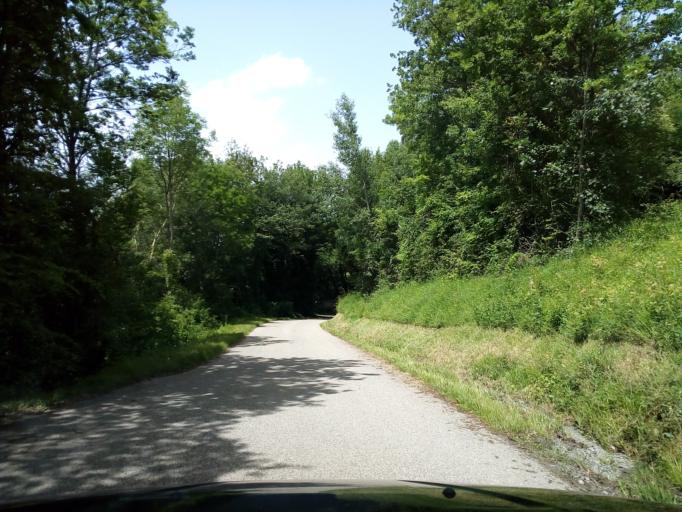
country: FR
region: Rhone-Alpes
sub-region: Departement de l'Isere
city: Herbeys
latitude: 45.1493
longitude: 5.7825
